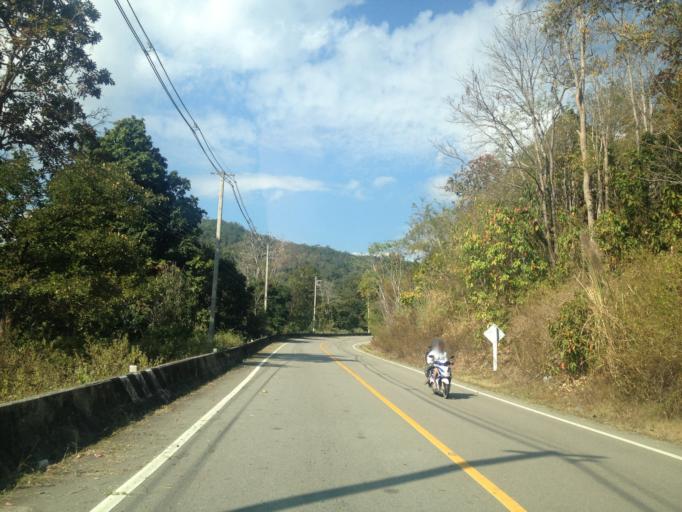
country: TH
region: Mae Hong Son
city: Ban Huai I Huak
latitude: 18.1337
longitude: 98.1816
